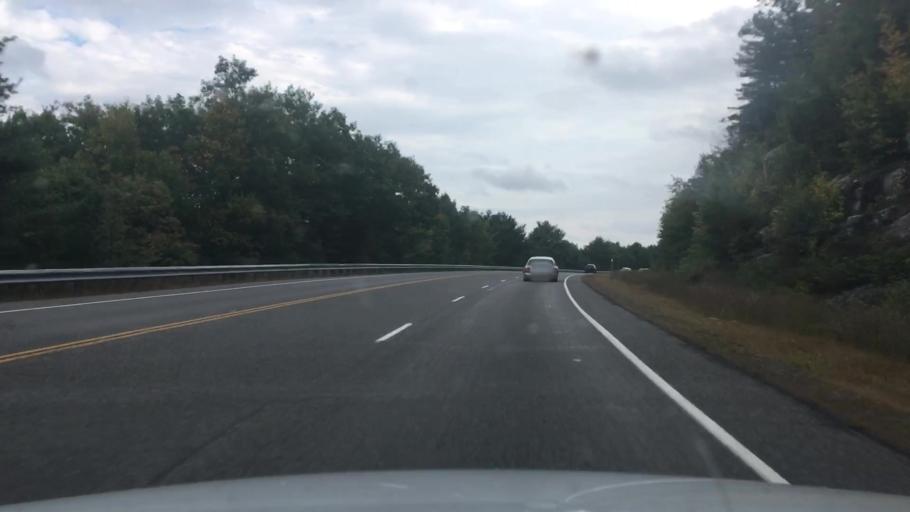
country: US
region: New Hampshire
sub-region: Carroll County
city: Wolfeboro
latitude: 43.5336
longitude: -71.2764
